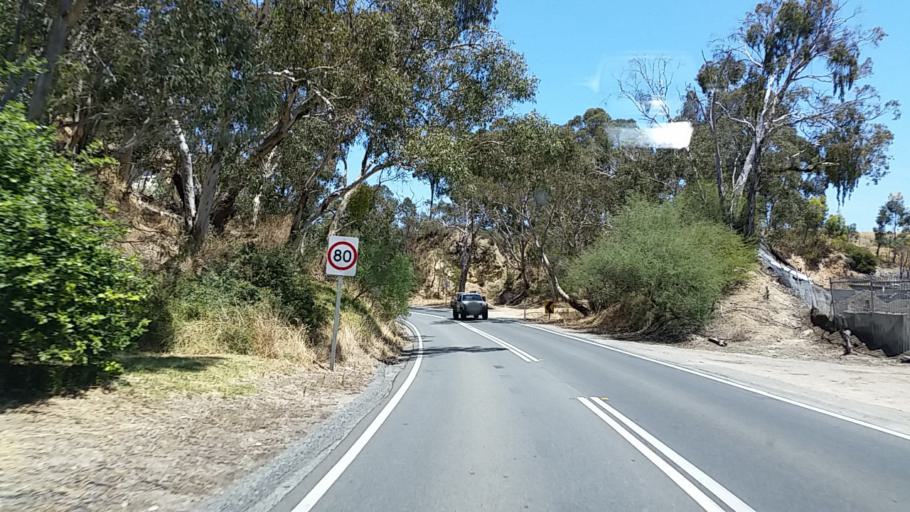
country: AU
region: South Australia
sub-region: Tea Tree Gully
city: Golden Grove
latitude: -34.8223
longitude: 138.7527
